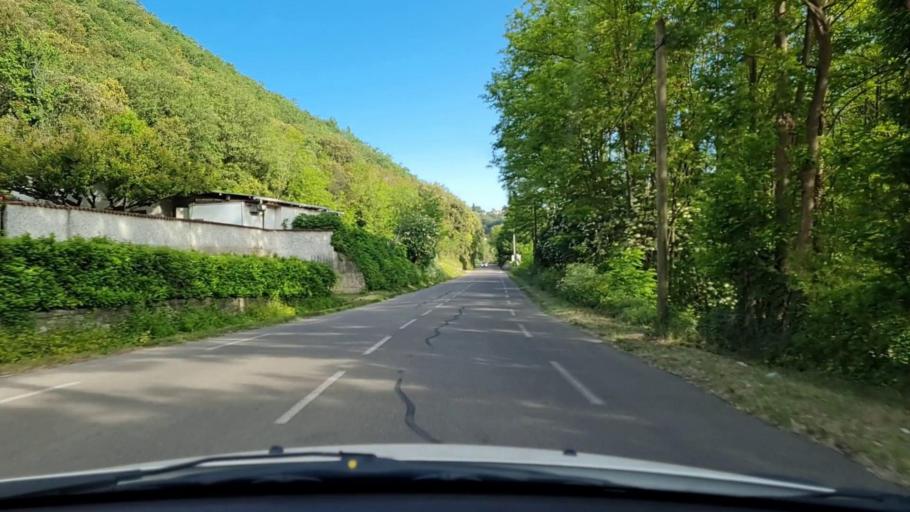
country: FR
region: Languedoc-Roussillon
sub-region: Departement du Gard
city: Cendras
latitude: 44.1443
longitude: 4.0634
